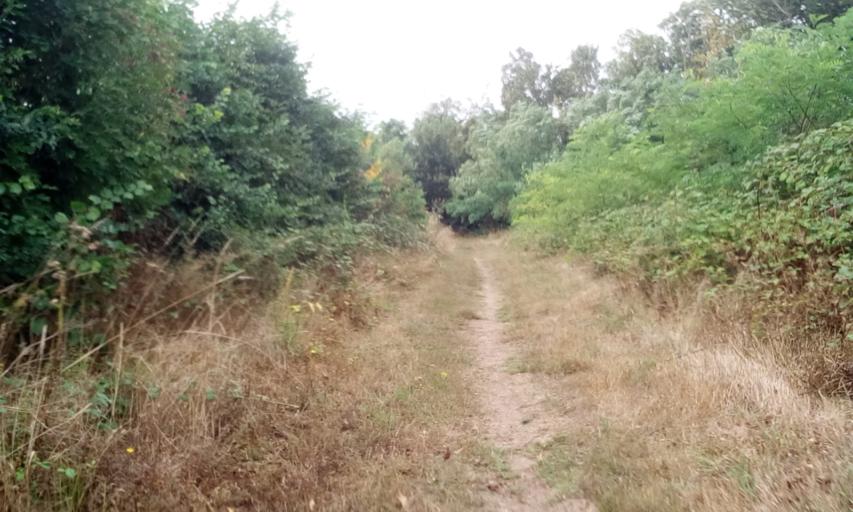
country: FR
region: Lower Normandy
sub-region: Departement du Calvados
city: Mouen
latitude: 49.1350
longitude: -0.4812
